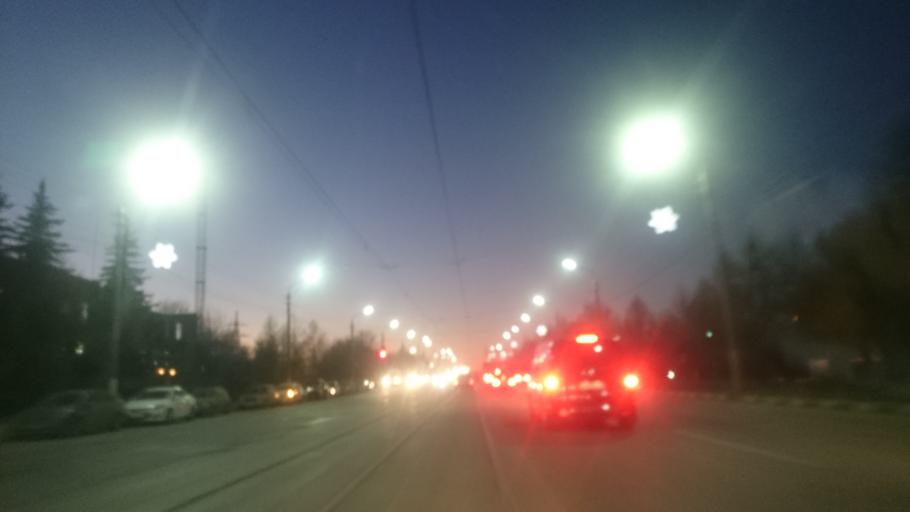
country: RU
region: Tula
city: Tula
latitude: 54.2011
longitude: 37.6294
